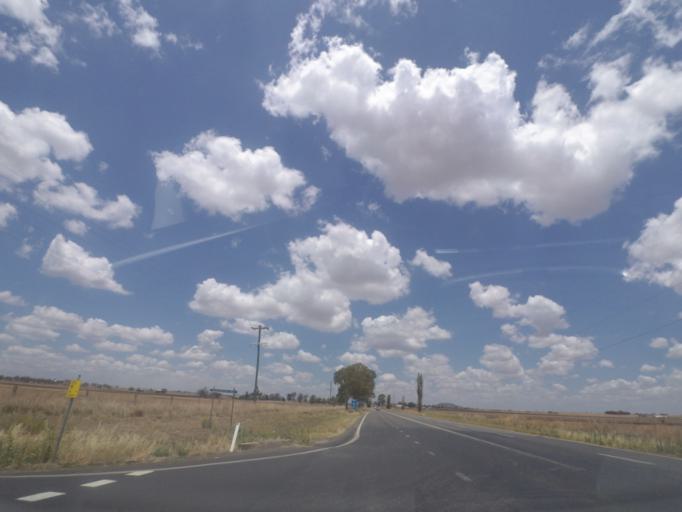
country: AU
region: Queensland
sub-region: Toowoomba
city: Top Camp
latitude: -27.9228
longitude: 151.9835
